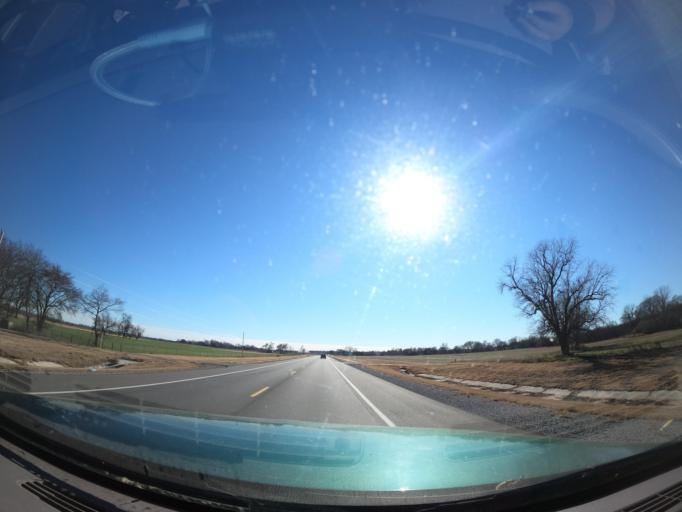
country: US
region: Oklahoma
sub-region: Wagoner County
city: Coweta
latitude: 35.8933
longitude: -95.6592
